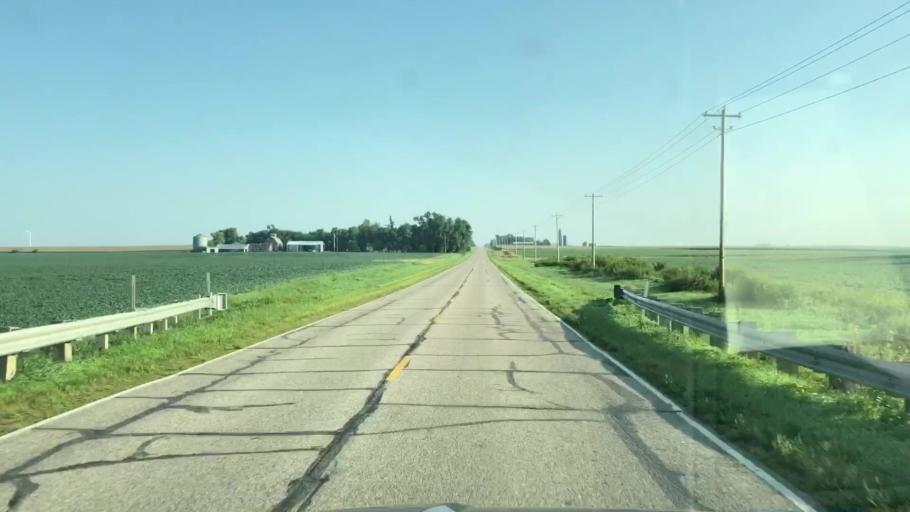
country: US
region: Iowa
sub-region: Lyon County
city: George
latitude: 43.3614
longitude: -95.9983
